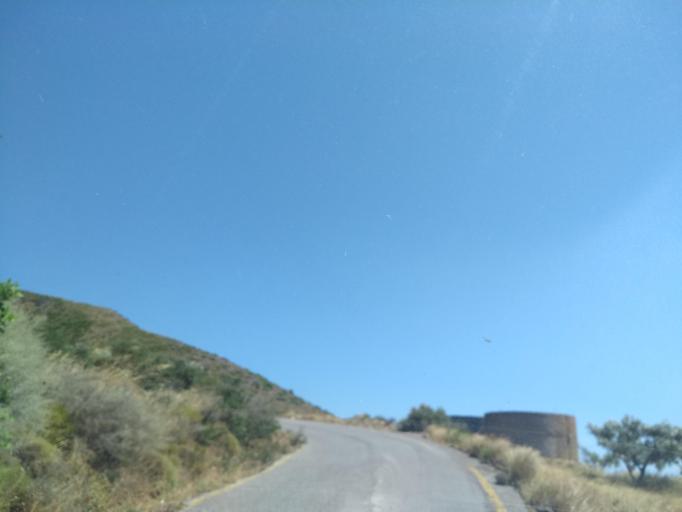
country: GR
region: Crete
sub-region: Nomos Chanias
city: Vryses
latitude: 35.3599
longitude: 23.5495
